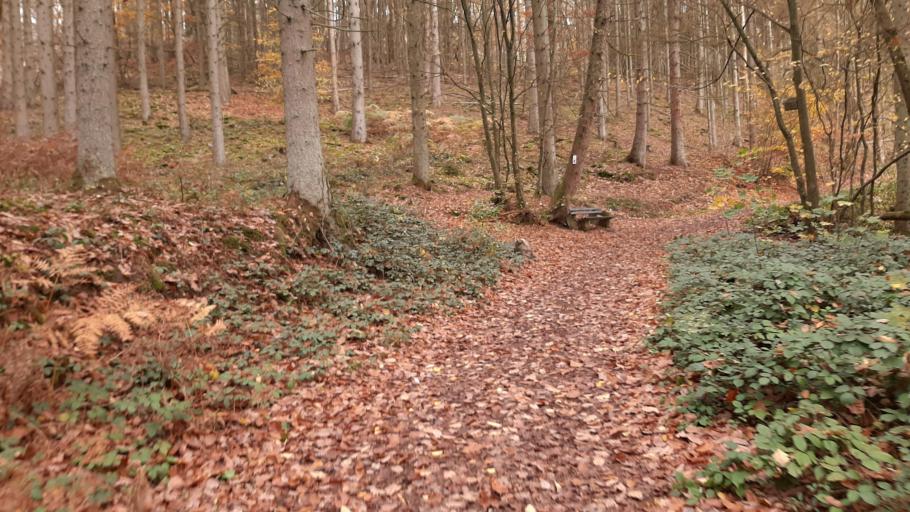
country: DE
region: Saarland
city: Orscholz
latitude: 49.4966
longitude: 6.5379
